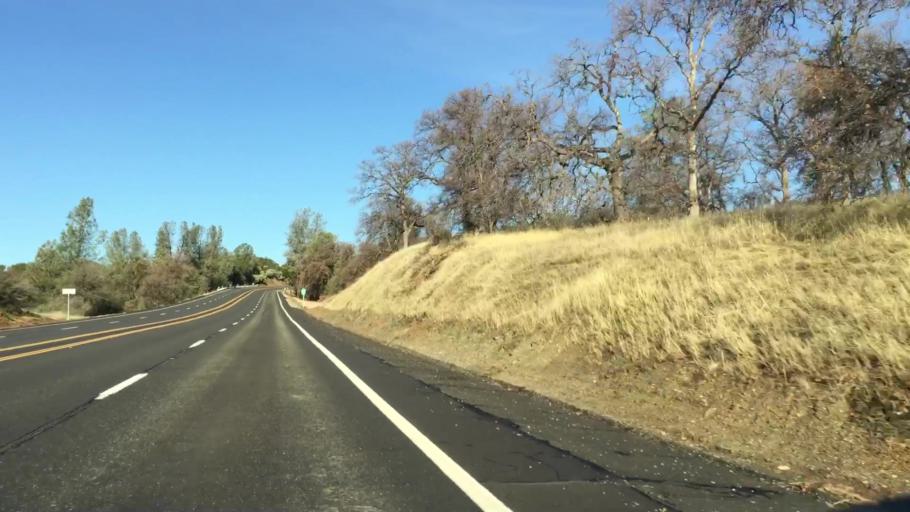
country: US
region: California
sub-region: Butte County
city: Paradise
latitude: 39.6793
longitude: -121.5362
